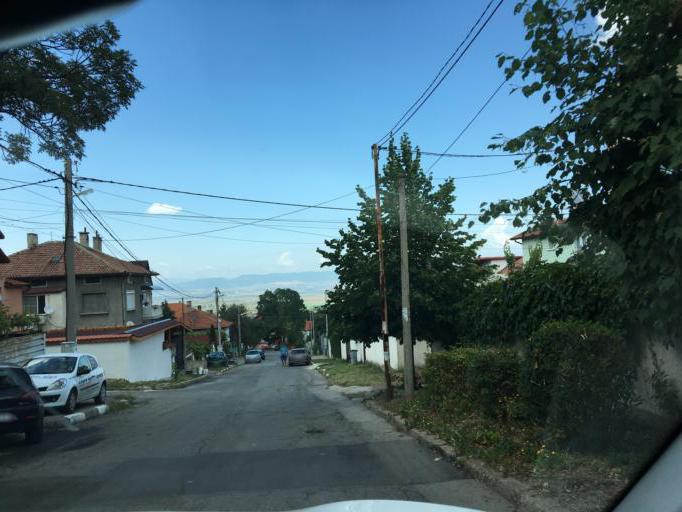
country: BG
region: Sofiya
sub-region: Obshtina Elin Pelin
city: Elin Pelin
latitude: 42.5994
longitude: 23.4763
